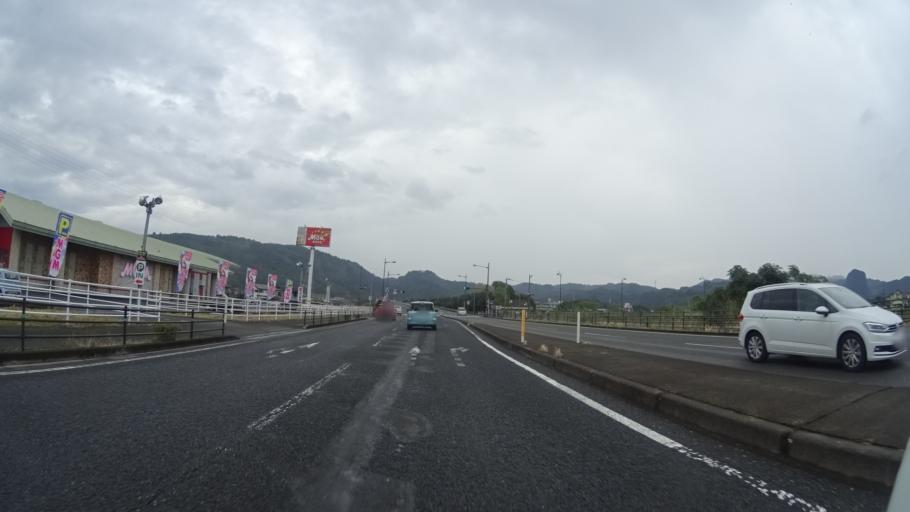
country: JP
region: Kagoshima
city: Kajiki
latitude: 31.7449
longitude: 130.6567
